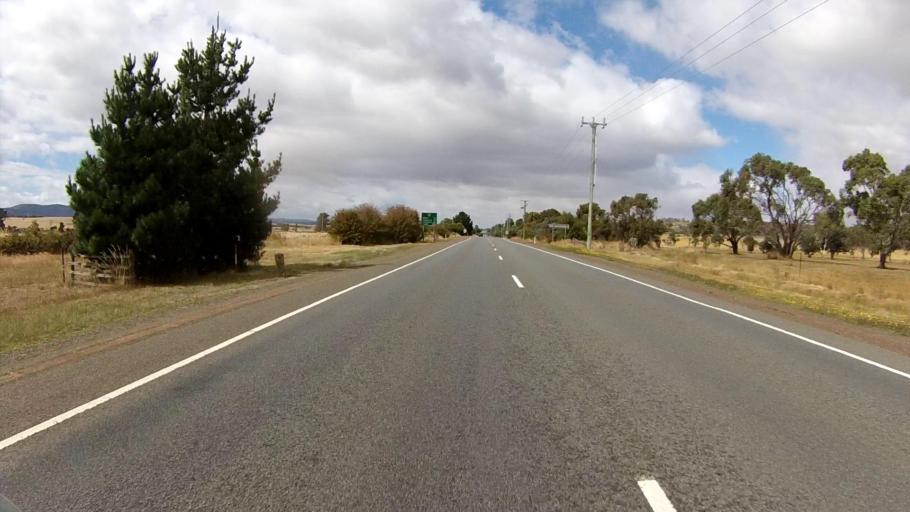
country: AU
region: Tasmania
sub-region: Northern Midlands
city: Evandale
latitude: -41.9445
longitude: 147.4926
